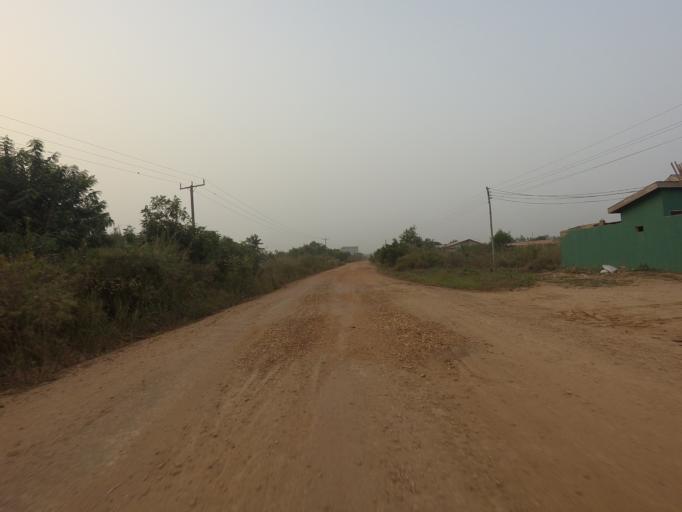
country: GH
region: Volta
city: Anloga
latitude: 5.9821
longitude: 0.6027
